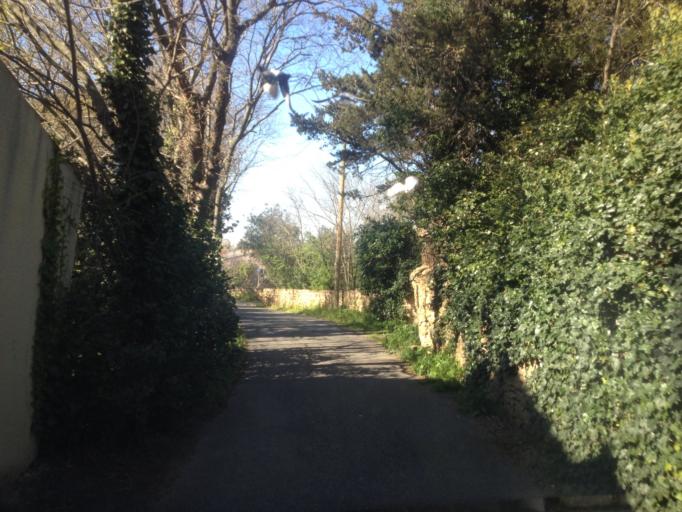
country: FR
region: Provence-Alpes-Cote d'Azur
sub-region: Departement du Vaucluse
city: Orange
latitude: 44.1254
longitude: 4.8202
